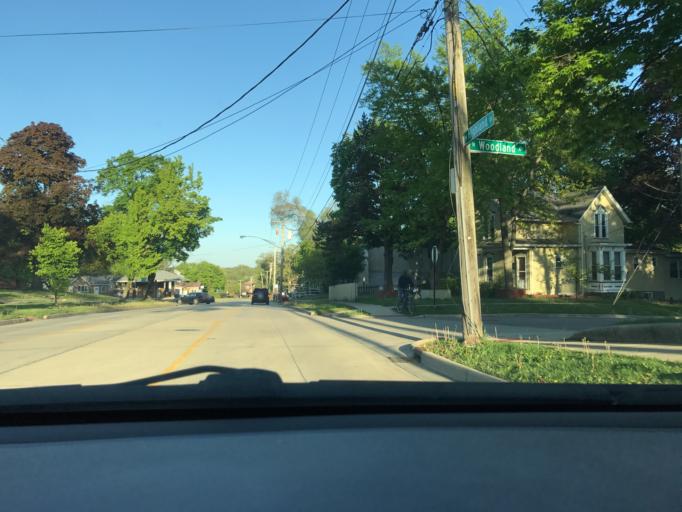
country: US
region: Illinois
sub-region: Kane County
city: Elgin
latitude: 42.0371
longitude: -88.2947
